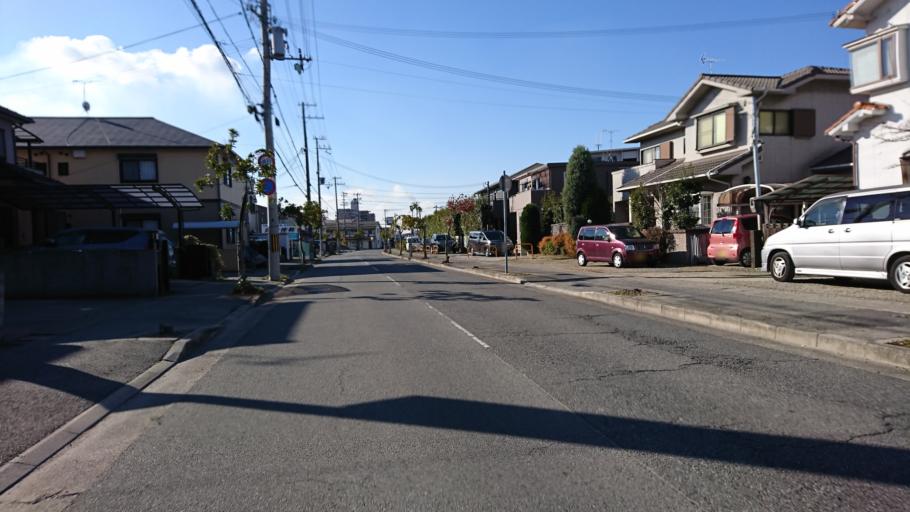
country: JP
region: Hyogo
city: Kakogawacho-honmachi
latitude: 34.7393
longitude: 134.8521
